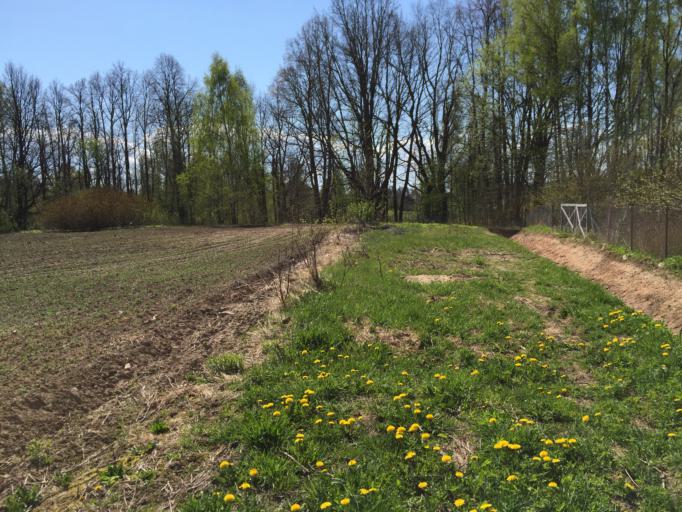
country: LV
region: Saulkrastu
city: Saulkrasti
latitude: 57.3256
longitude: 24.4765
